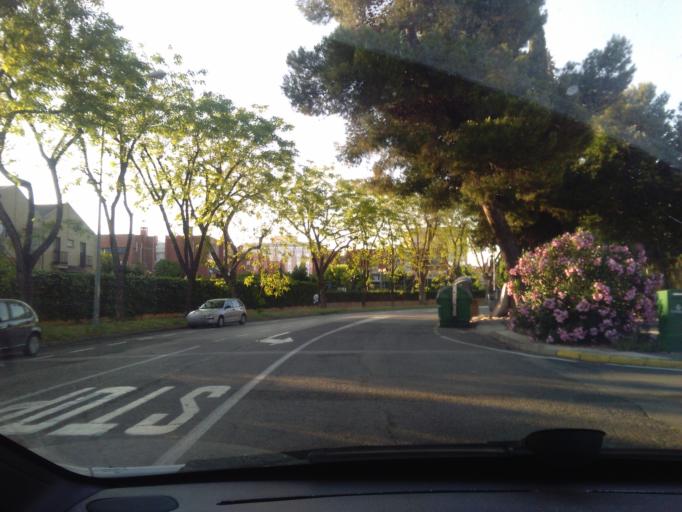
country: ES
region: Andalusia
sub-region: Provincia de Sevilla
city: Sevilla
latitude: 37.4058
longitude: -5.9460
